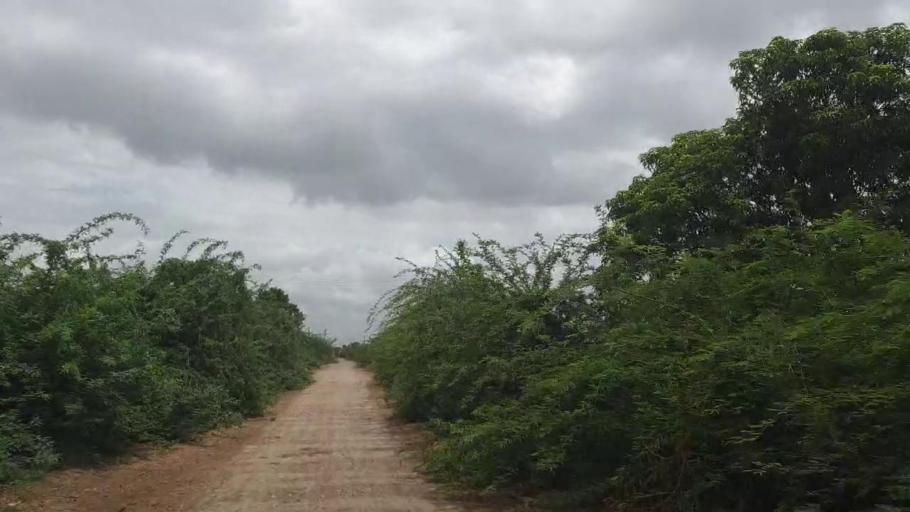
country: PK
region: Sindh
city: Badin
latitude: 24.6286
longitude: 68.9468
